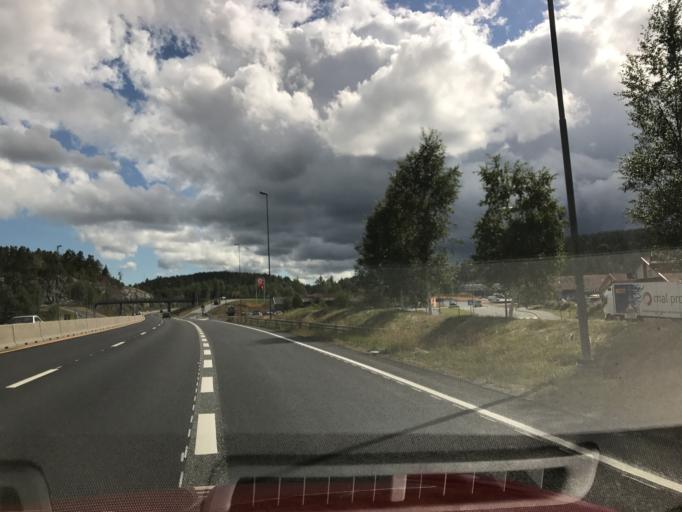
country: NO
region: Aust-Agder
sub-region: Gjerstad
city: Gjerstad
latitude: 58.8235
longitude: 9.0756
